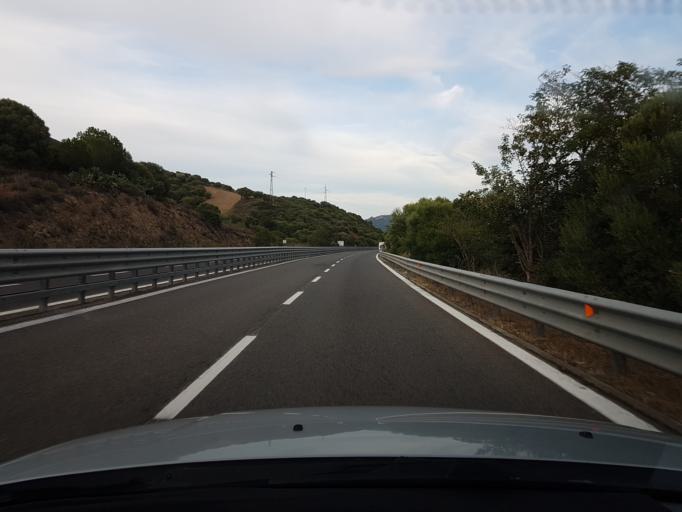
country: IT
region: Sardinia
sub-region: Provincia di Nuoro
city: Orune
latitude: 40.3685
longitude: 9.3764
